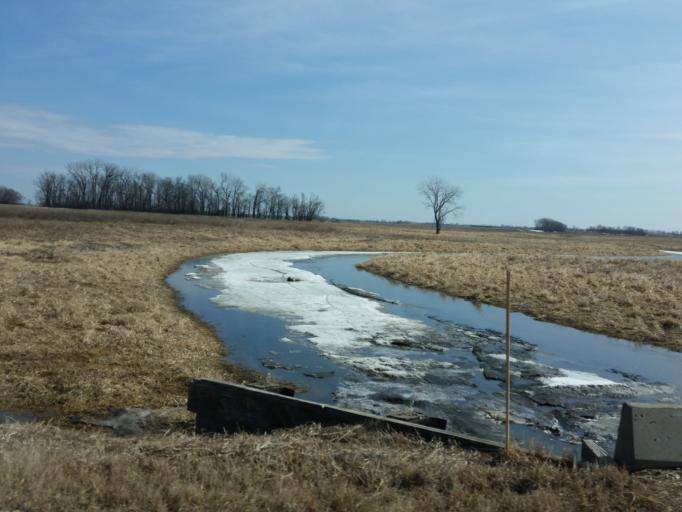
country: US
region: North Dakota
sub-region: Walsh County
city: Grafton
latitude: 48.3004
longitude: -97.2110
